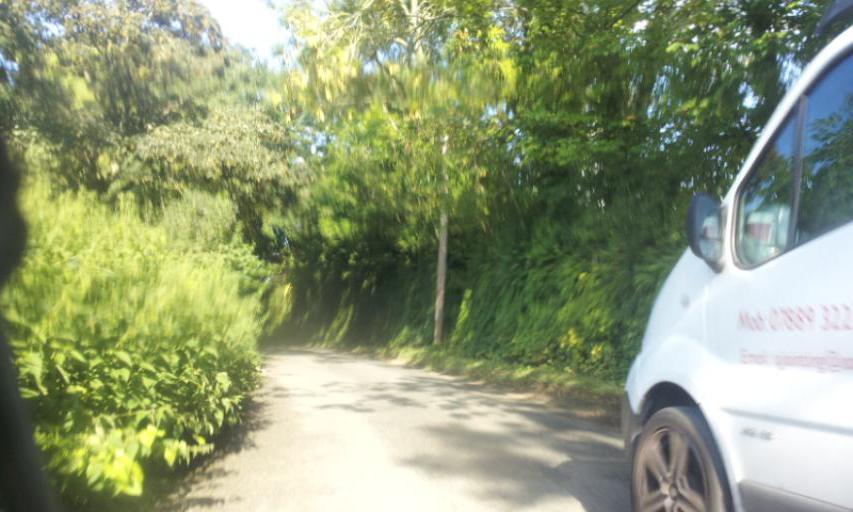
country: GB
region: England
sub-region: Kent
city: Hadlow
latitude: 51.2503
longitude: 0.3611
